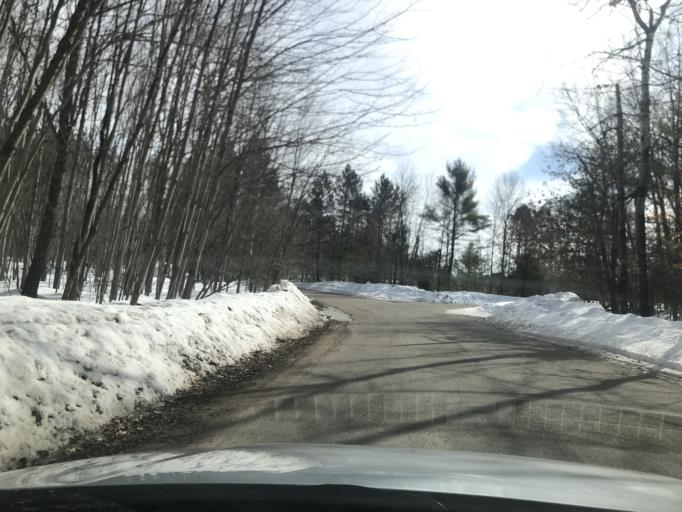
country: US
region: Wisconsin
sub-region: Menominee County
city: Legend Lake
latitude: 45.1134
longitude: -88.4435
